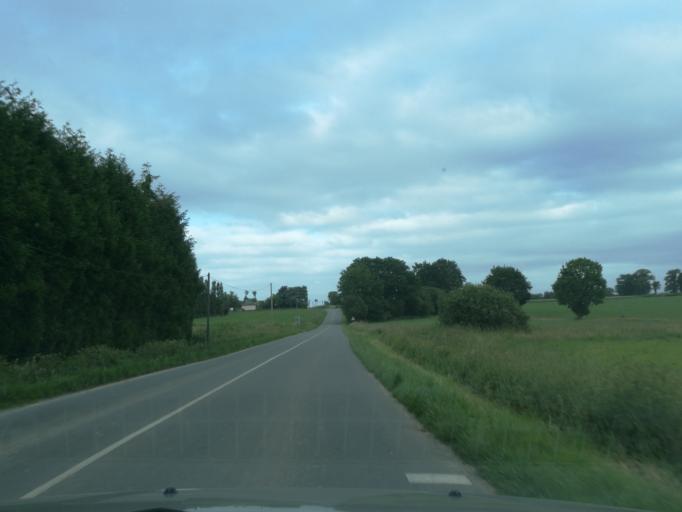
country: FR
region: Brittany
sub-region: Departement d'Ille-et-Vilaine
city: Bedee
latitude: 48.2058
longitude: -1.9686
